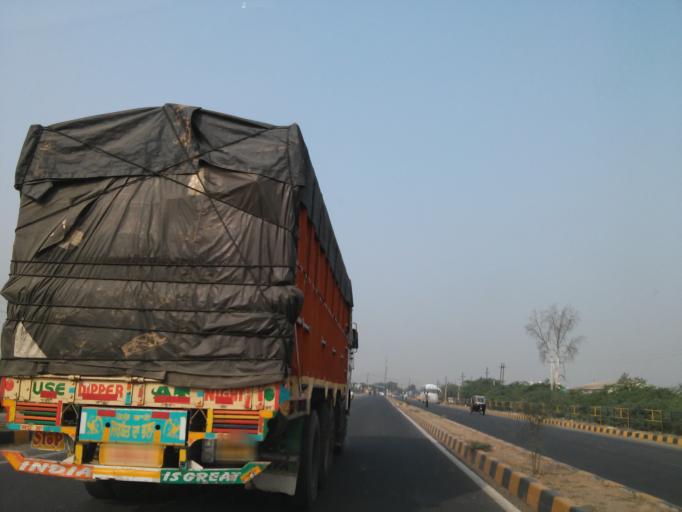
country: IN
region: Gujarat
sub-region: Kachchh
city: Bhuj
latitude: 23.2362
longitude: 69.7280
